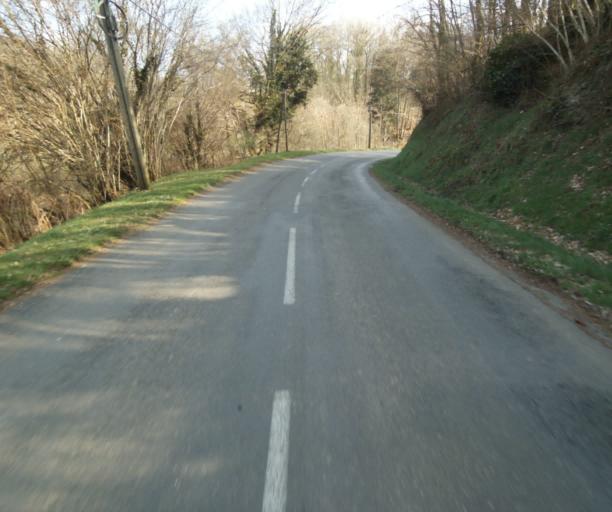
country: FR
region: Limousin
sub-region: Departement de la Correze
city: Saint-Clement
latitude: 45.3463
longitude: 1.6249
